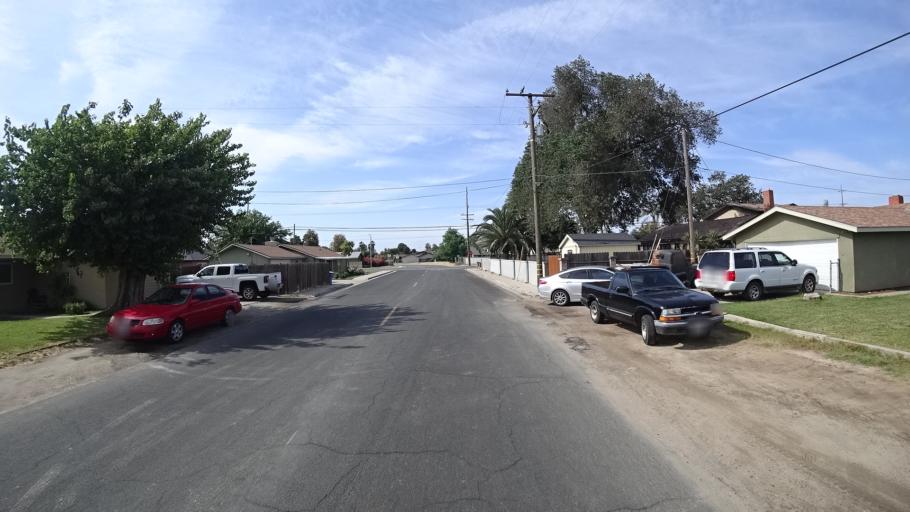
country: US
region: California
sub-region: Kings County
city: Hanford
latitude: 36.3141
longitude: -119.6639
